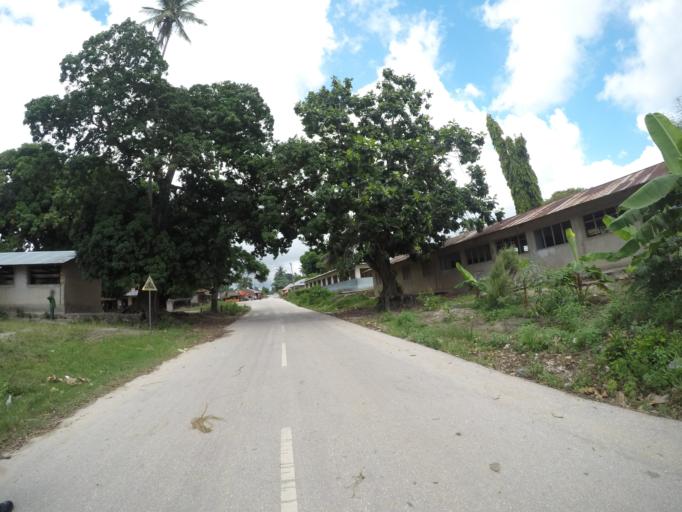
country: TZ
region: Pemba South
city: Mtambile
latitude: -5.3846
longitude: 39.7435
